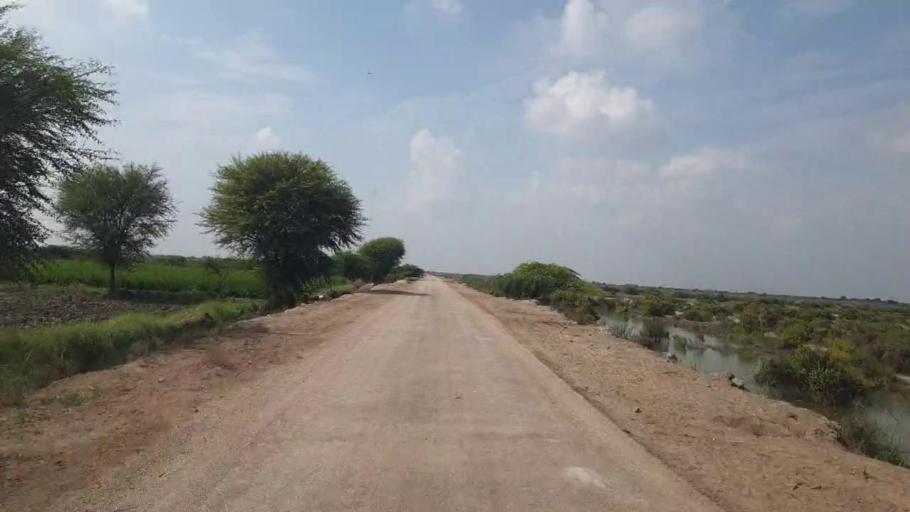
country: PK
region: Sindh
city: Badin
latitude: 24.5066
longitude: 68.6168
